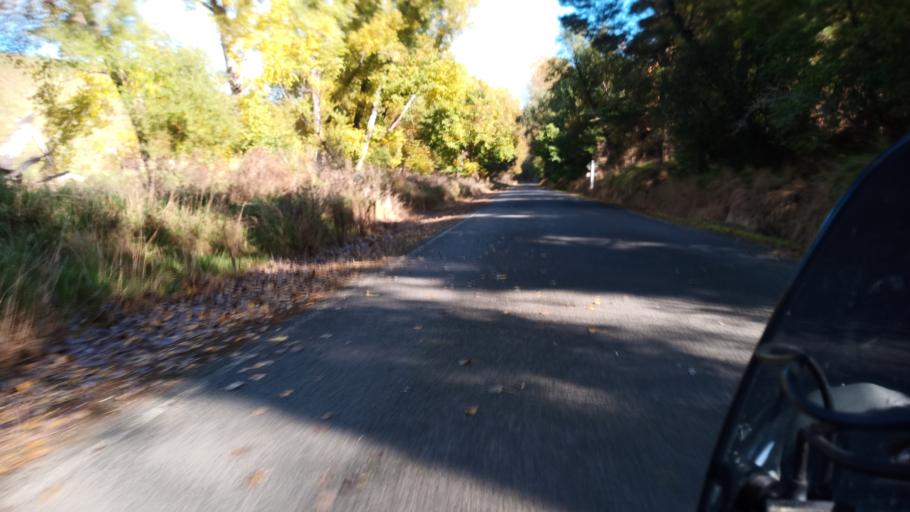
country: NZ
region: Hawke's Bay
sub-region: Wairoa District
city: Wairoa
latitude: -38.9202
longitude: 177.2532
